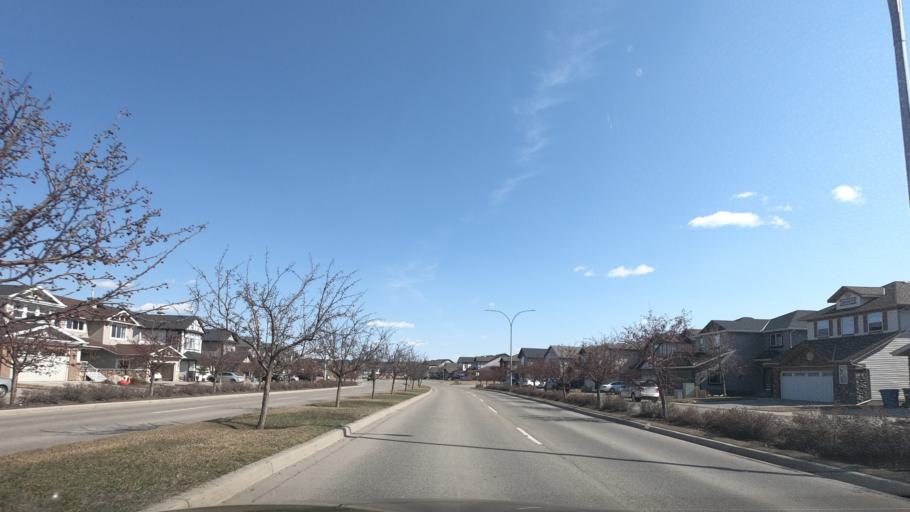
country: CA
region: Alberta
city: Airdrie
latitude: 51.2669
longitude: -113.9875
